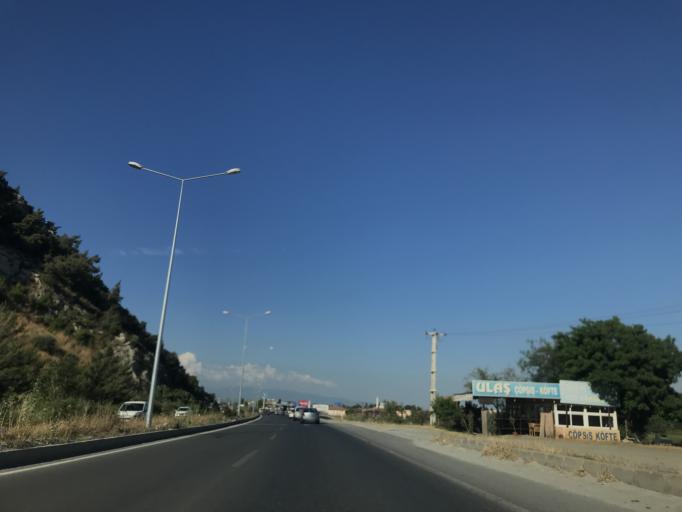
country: TR
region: Aydin
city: Soeke
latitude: 37.7751
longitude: 27.4445
